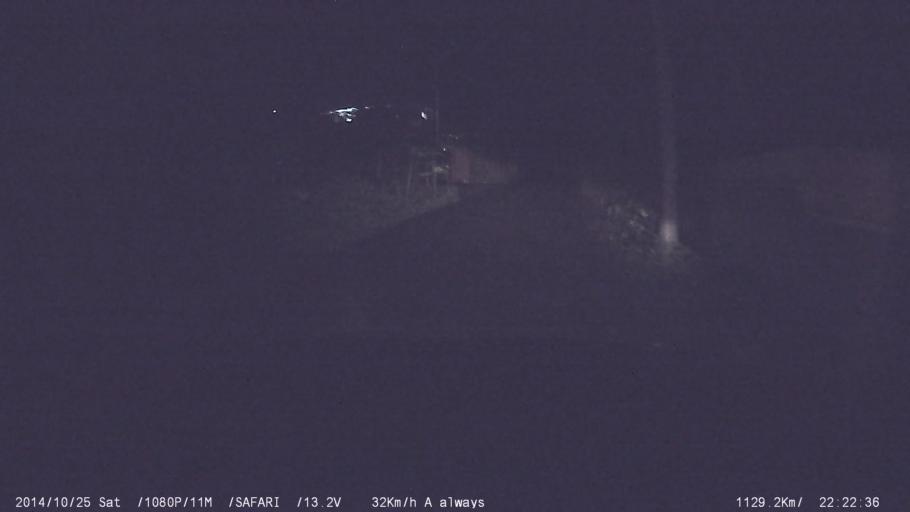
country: IN
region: Kerala
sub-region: Kottayam
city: Palackattumala
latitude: 9.7649
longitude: 76.5656
